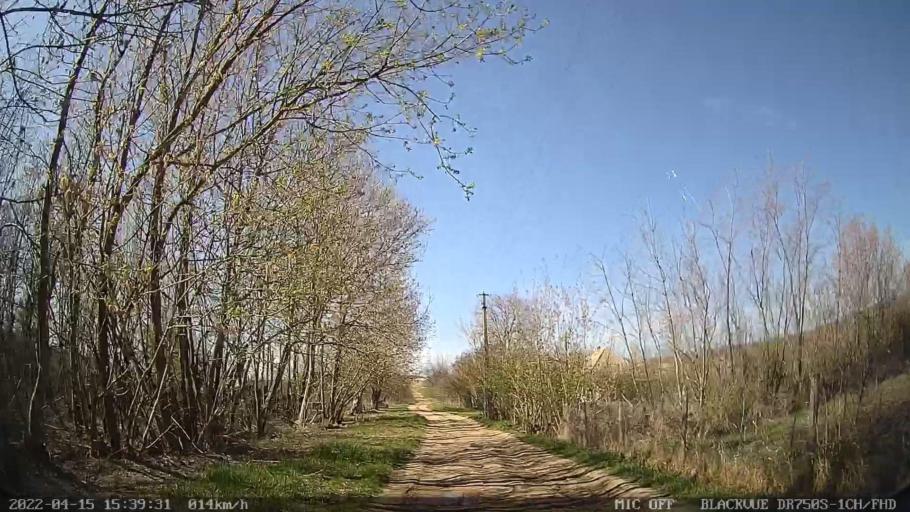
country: MD
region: Raionul Ocnita
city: Otaci
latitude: 48.3537
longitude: 27.9271
